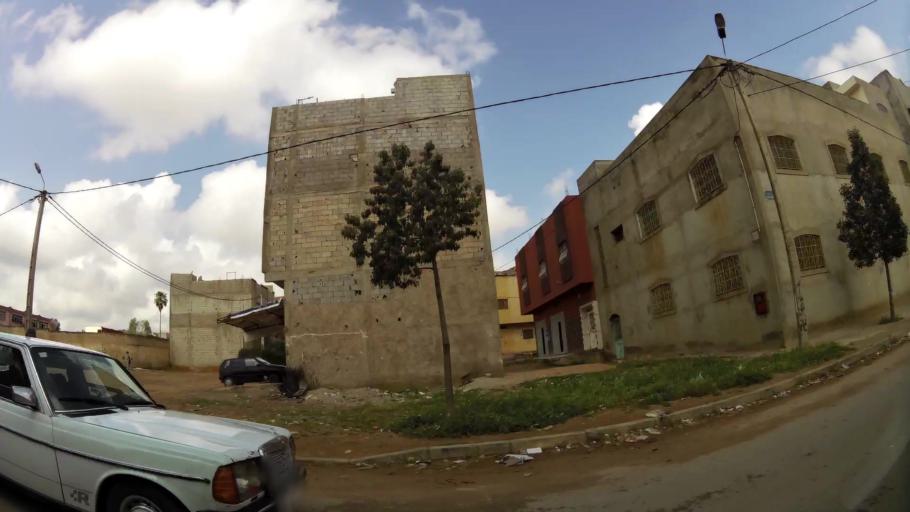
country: MA
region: Rabat-Sale-Zemmour-Zaer
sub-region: Khemisset
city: Tiflet
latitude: 33.8965
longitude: -6.3233
